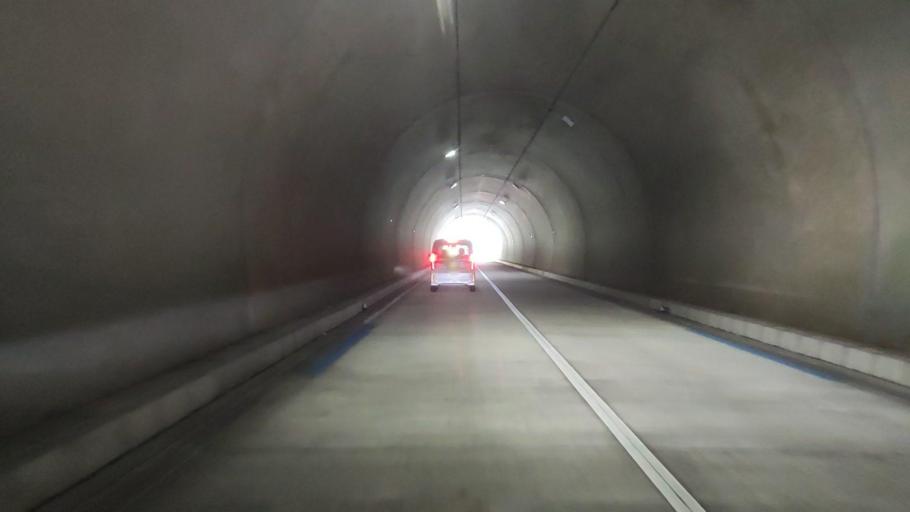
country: JP
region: Wakayama
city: Shingu
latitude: 33.8900
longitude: 135.8798
